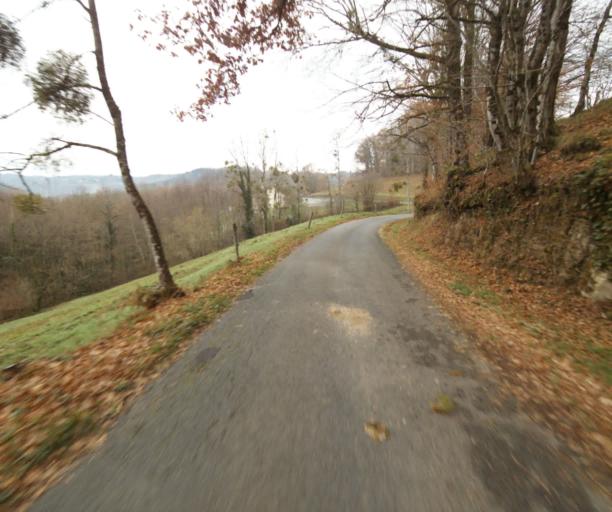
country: FR
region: Limousin
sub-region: Departement de la Correze
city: Tulle
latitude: 45.2350
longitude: 1.7405
